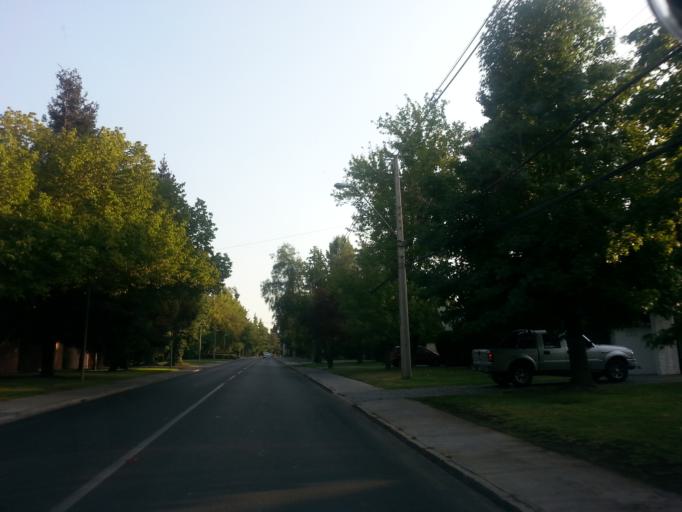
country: CL
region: Santiago Metropolitan
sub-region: Provincia de Santiago
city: Villa Presidente Frei, Nunoa, Santiago, Chile
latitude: -33.3961
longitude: -70.5314
